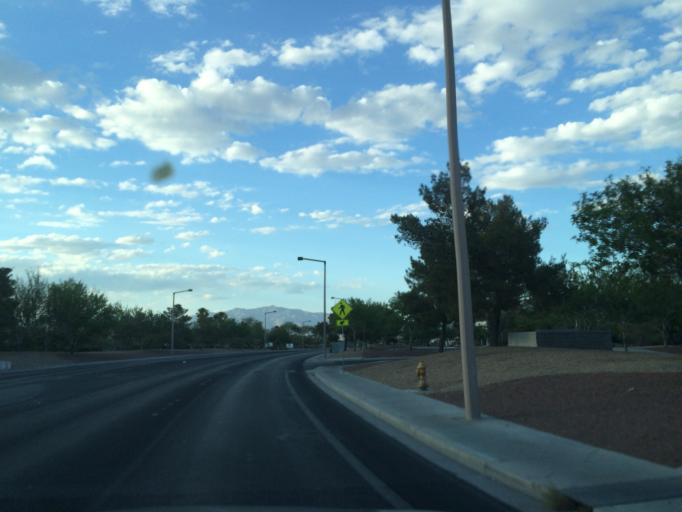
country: US
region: Nevada
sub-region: Clark County
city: Spring Valley
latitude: 36.2059
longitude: -115.2513
